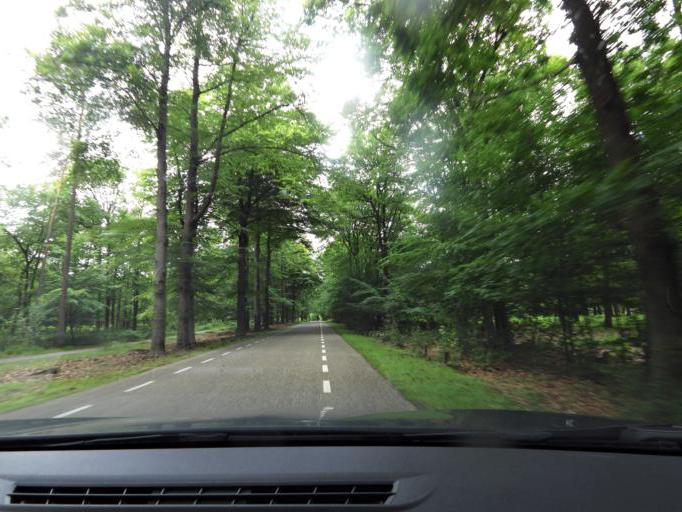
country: NL
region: Gelderland
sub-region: Gemeente Apeldoorn
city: Uddel
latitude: 52.2445
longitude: 5.8243
